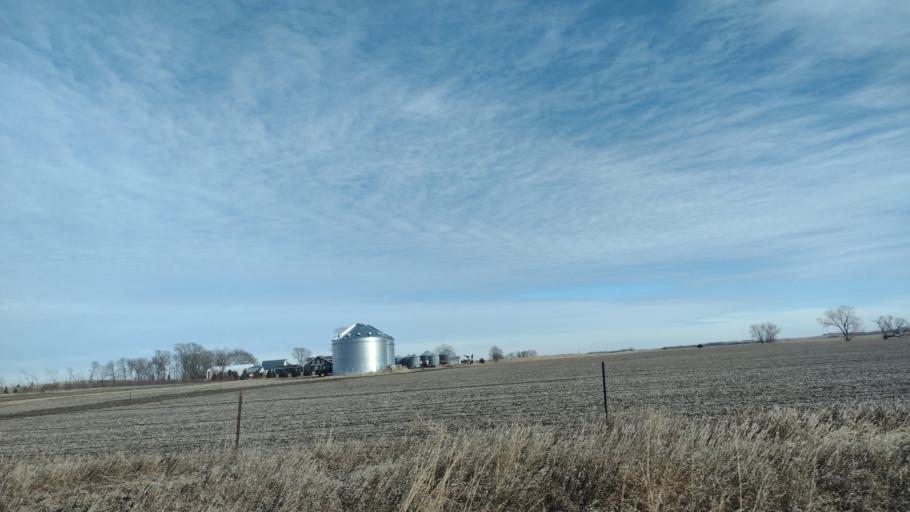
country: US
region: South Dakota
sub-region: Union County
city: Beresford
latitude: 42.9495
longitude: -96.8055
